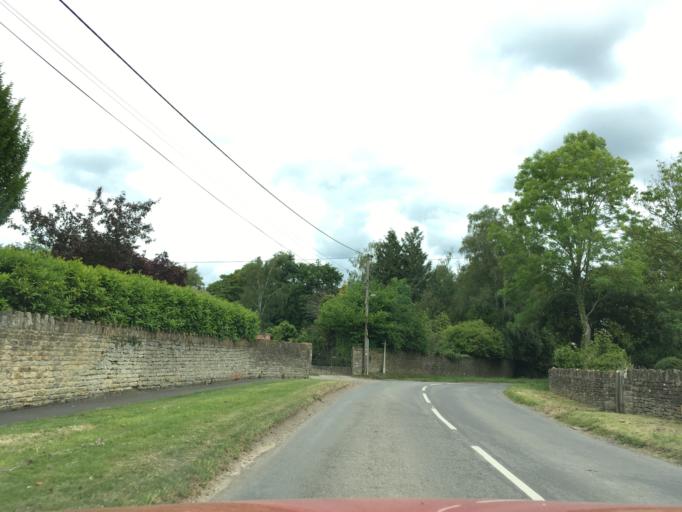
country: GB
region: England
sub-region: Wiltshire
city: Charlton
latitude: 51.5576
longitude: -2.0497
